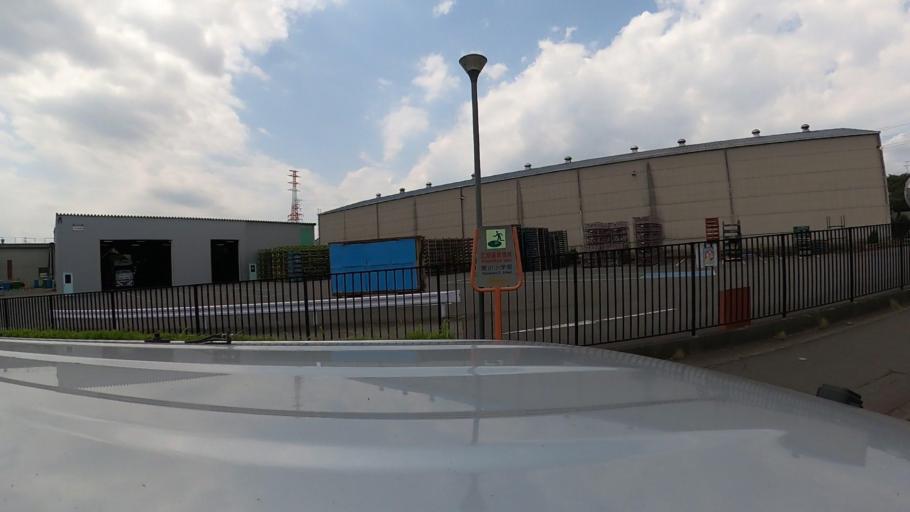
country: JP
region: Kanagawa
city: Chigasaki
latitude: 35.3727
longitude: 139.3940
